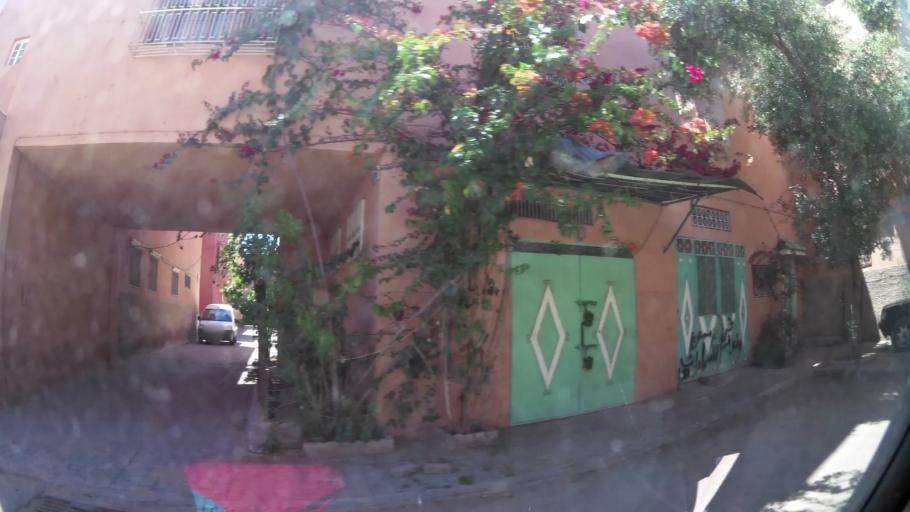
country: MA
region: Marrakech-Tensift-Al Haouz
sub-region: Marrakech
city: Marrakesh
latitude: 31.6561
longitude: -8.0011
